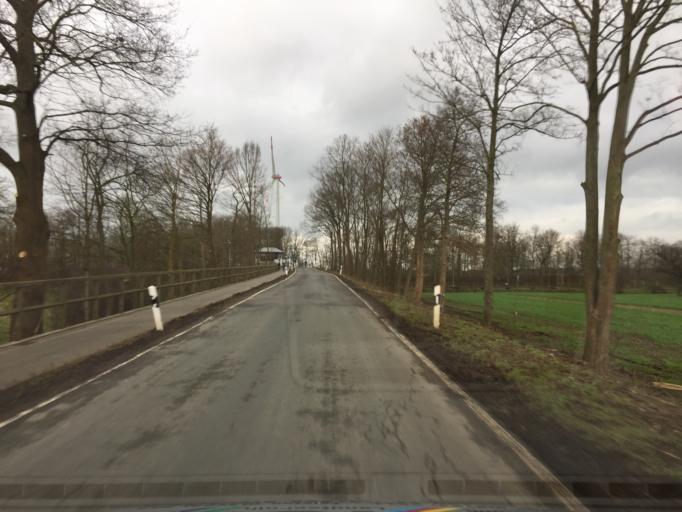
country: DE
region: Lower Saxony
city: Stolzenau
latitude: 52.4933
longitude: 9.0619
